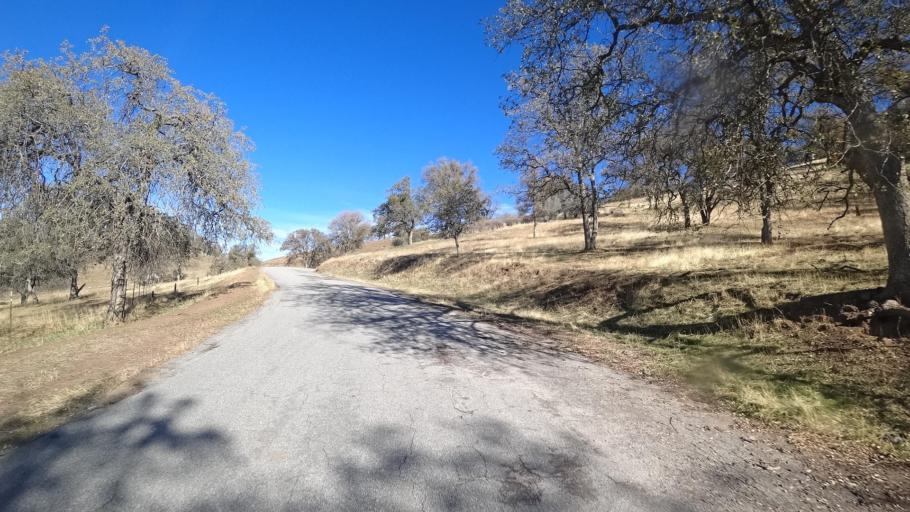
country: US
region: California
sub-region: Kern County
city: Bodfish
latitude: 35.4405
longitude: -118.6920
